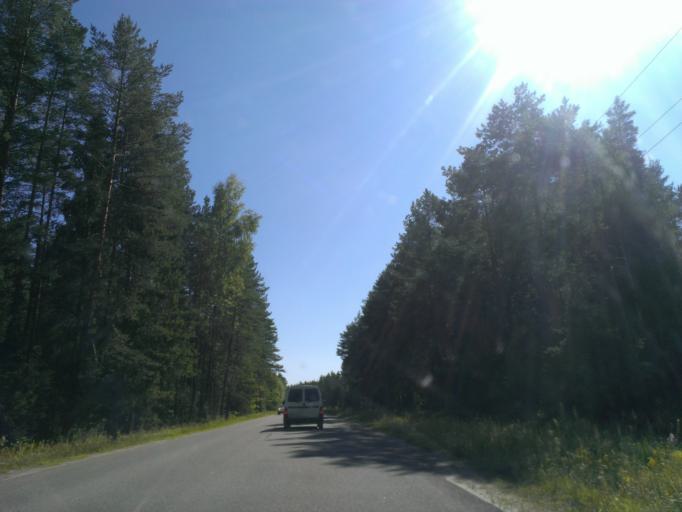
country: LV
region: Sigulda
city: Sigulda
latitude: 57.1174
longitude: 24.8260
